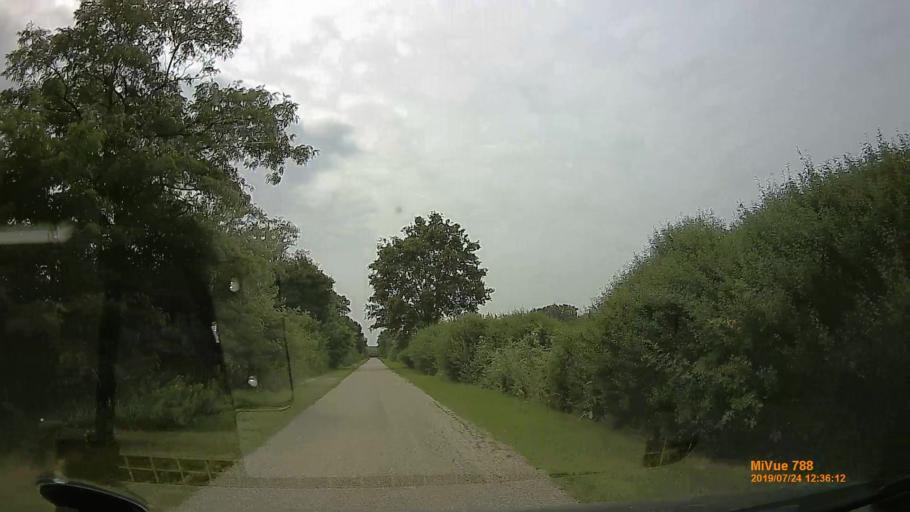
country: HU
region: Szabolcs-Szatmar-Bereg
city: Vasarosnameny
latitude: 48.1923
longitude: 22.3415
